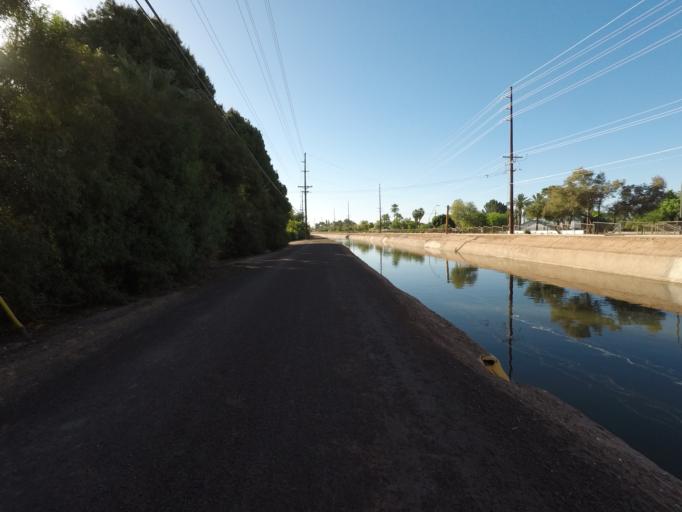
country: US
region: Arizona
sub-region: Maricopa County
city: Paradise Valley
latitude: 33.4936
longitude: -111.9721
